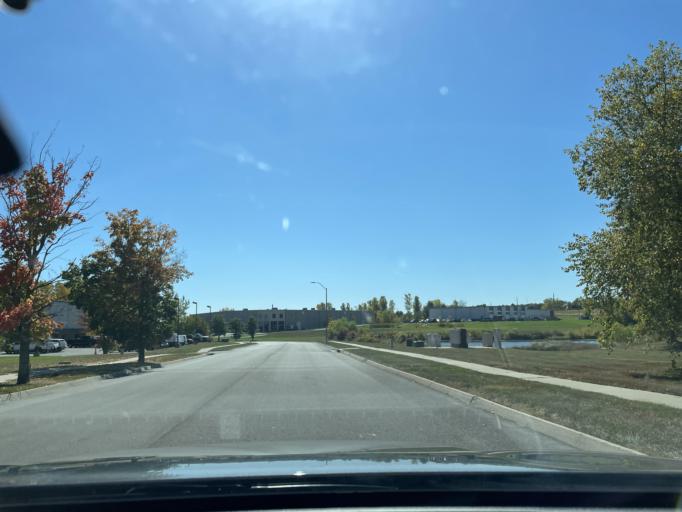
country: US
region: Missouri
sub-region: Buchanan County
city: Saint Joseph
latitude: 39.7535
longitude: -94.7648
